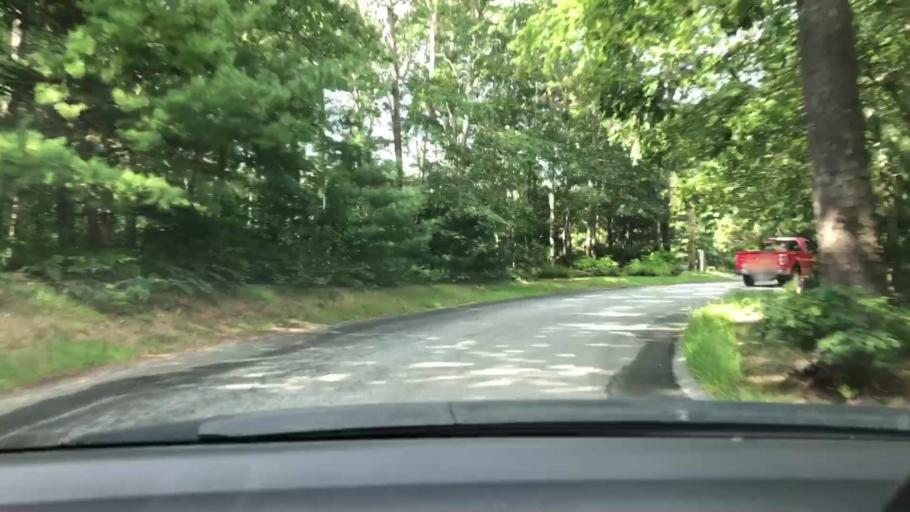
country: US
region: Massachusetts
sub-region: Plymouth County
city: Plymouth
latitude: 41.8938
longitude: -70.5929
